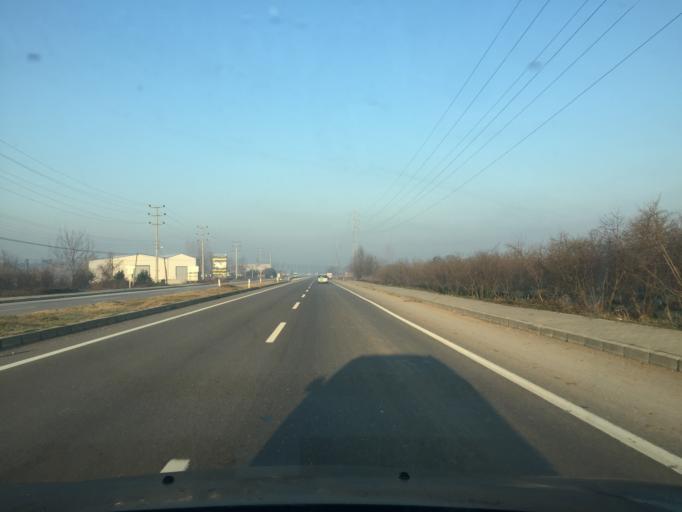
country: TR
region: Sakarya
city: Akyazi
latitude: 40.6368
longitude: 30.6230
